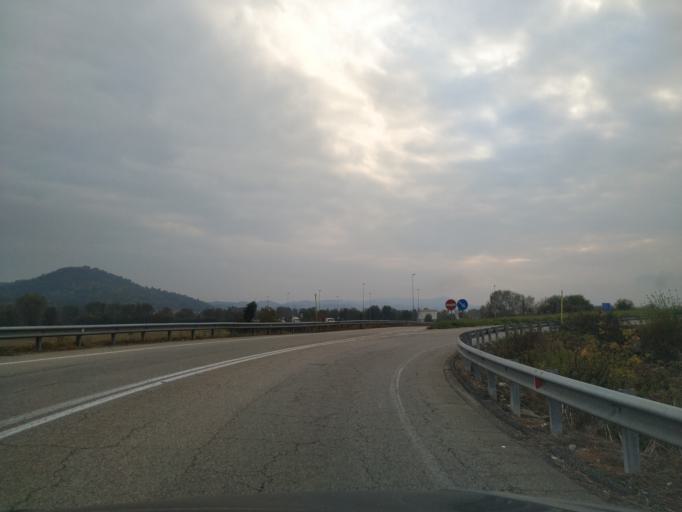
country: IT
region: Piedmont
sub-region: Provincia di Torino
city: Brandizzo
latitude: 45.1860
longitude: 7.8604
